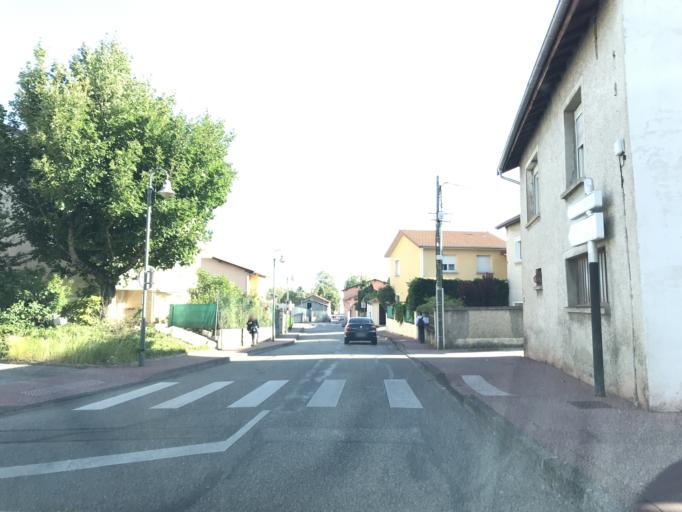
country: FR
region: Rhone-Alpes
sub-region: Departement du Rhone
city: Mions
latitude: 45.6627
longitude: 4.9591
